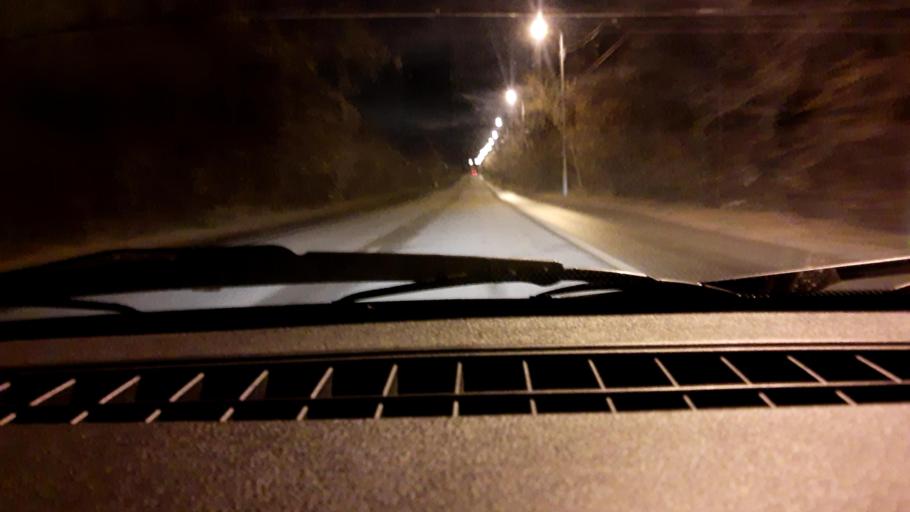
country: RU
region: Bashkortostan
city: Blagoveshchensk
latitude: 54.8922
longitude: 56.0533
